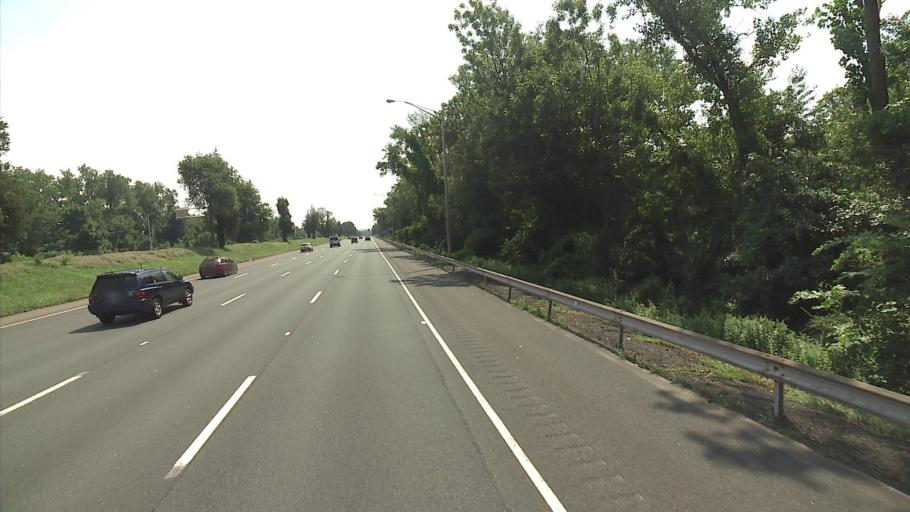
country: US
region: Connecticut
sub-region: Hartford County
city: Manchester
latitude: 41.7644
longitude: -72.5641
